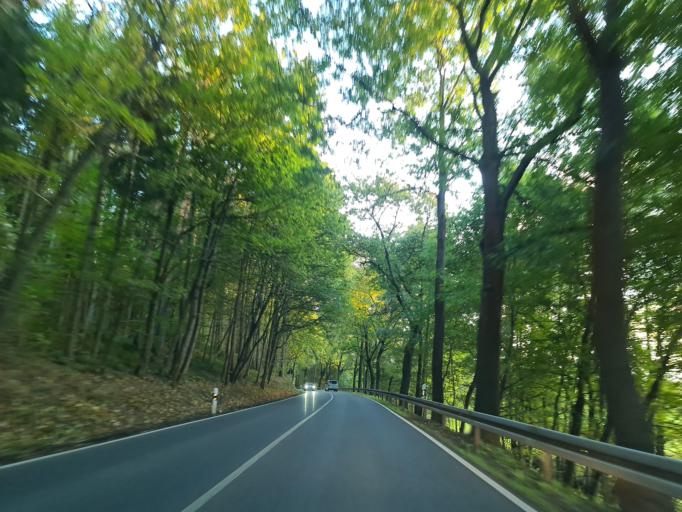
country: DE
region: Saxony
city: Elsterberg
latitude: 50.5729
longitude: 12.1276
